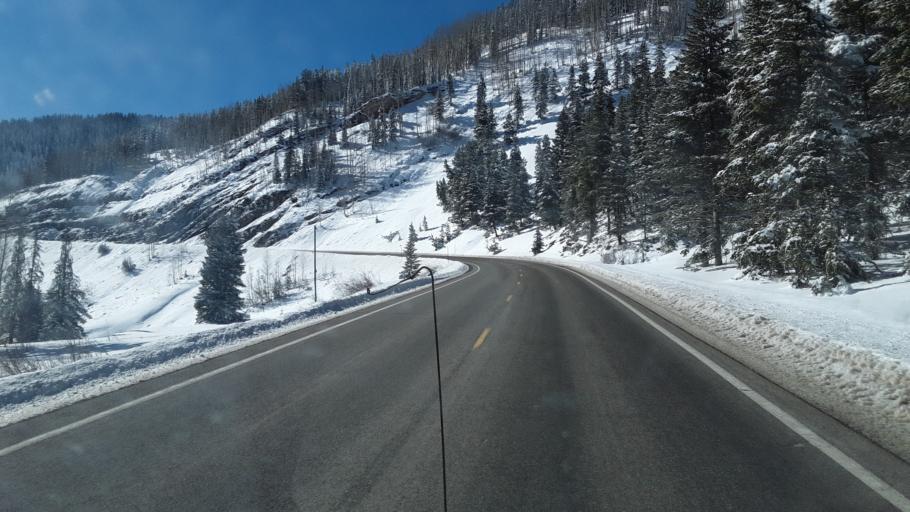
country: US
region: Colorado
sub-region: San Juan County
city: Silverton
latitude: 37.7119
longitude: -107.7612
